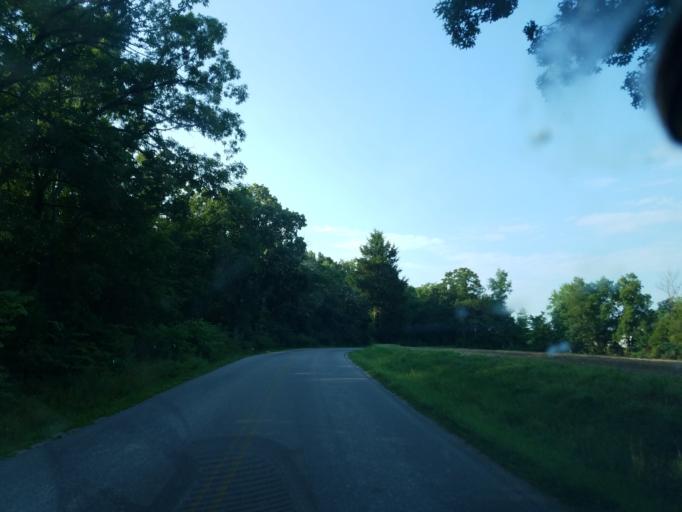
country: US
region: Ohio
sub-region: Adams County
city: West Union
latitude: 38.9009
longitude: -83.5202
